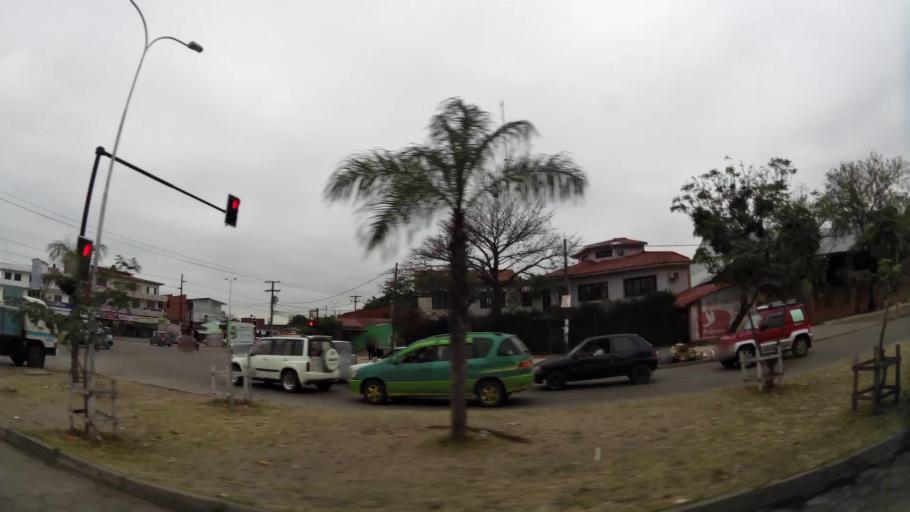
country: BO
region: Santa Cruz
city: Santa Cruz de la Sierra
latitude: -17.7777
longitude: -63.2031
